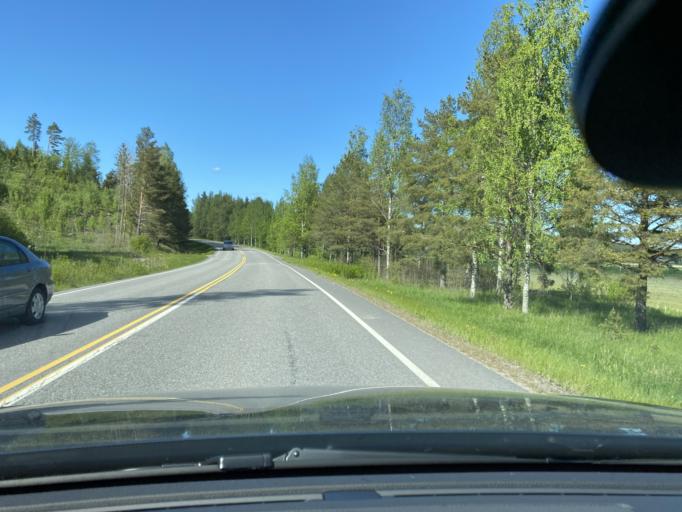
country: FI
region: Varsinais-Suomi
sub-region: Turku
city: Sauvo
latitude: 60.3647
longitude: 22.6741
